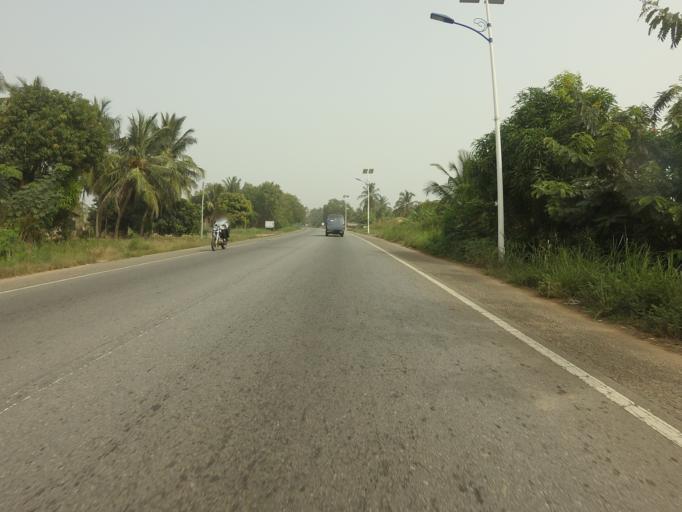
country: GH
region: Volta
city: Anloga
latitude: 5.9908
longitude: 0.5730
